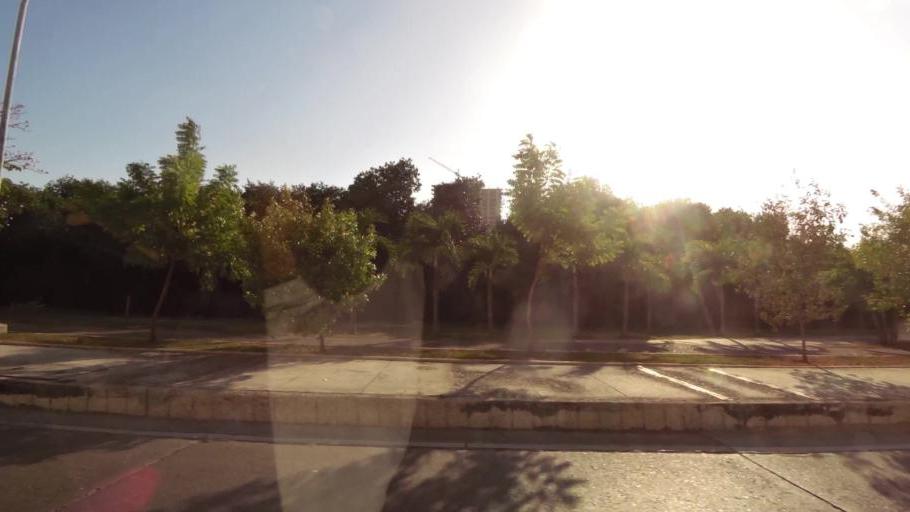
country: CO
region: Bolivar
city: Cartagena
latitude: 10.4178
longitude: -75.5349
